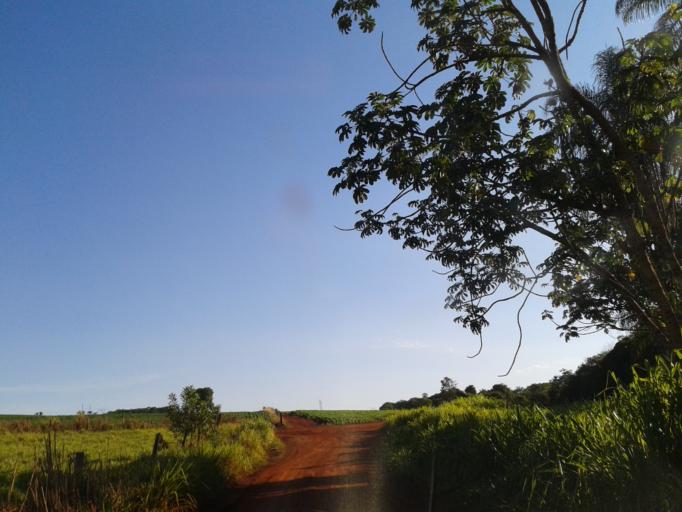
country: BR
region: Minas Gerais
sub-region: Centralina
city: Centralina
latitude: -18.6838
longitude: -49.2826
